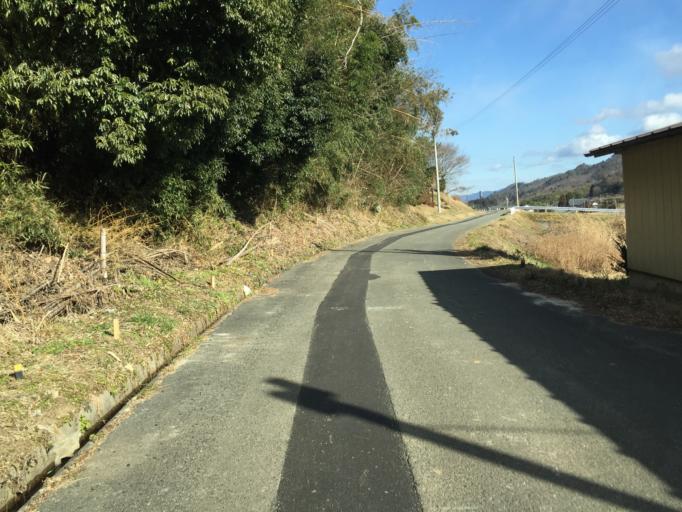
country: JP
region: Fukushima
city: Hobaramachi
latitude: 37.7392
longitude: 140.5568
